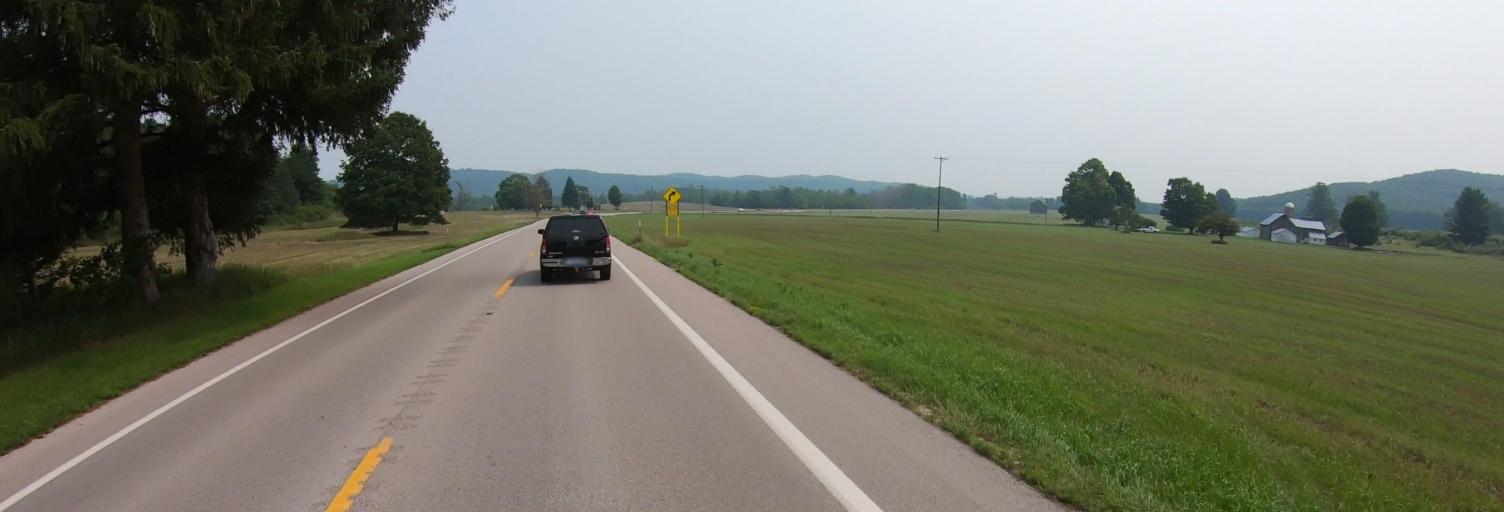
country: US
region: Michigan
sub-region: Leelanau County
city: Leland
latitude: 44.9362
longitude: -85.9397
